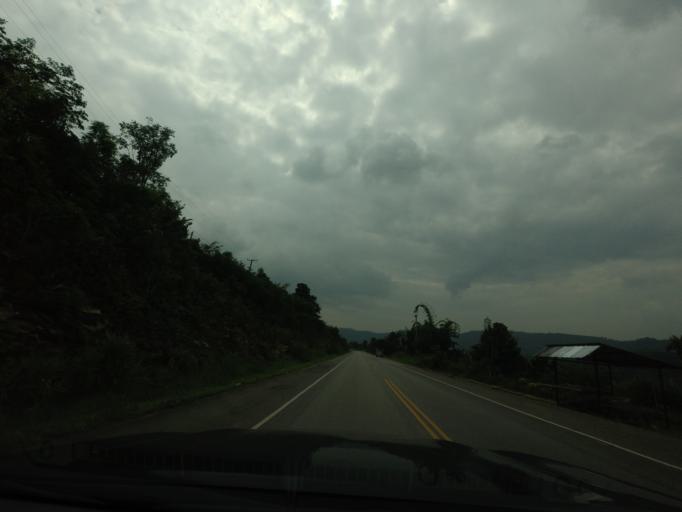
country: TH
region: Loei
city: Dan Sai
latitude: 17.2189
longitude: 101.1796
